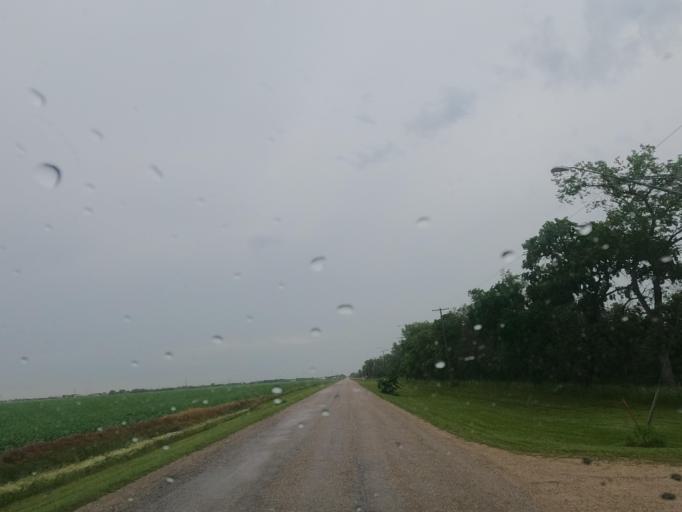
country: CA
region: Manitoba
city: Winnipeg
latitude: 49.8273
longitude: -96.9812
